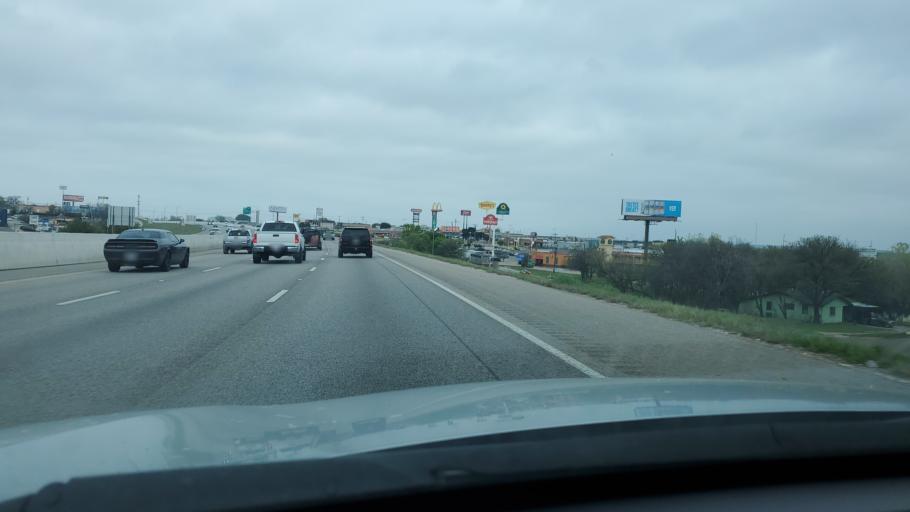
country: US
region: Texas
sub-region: Bell County
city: Killeen
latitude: 31.1074
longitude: -97.7451
